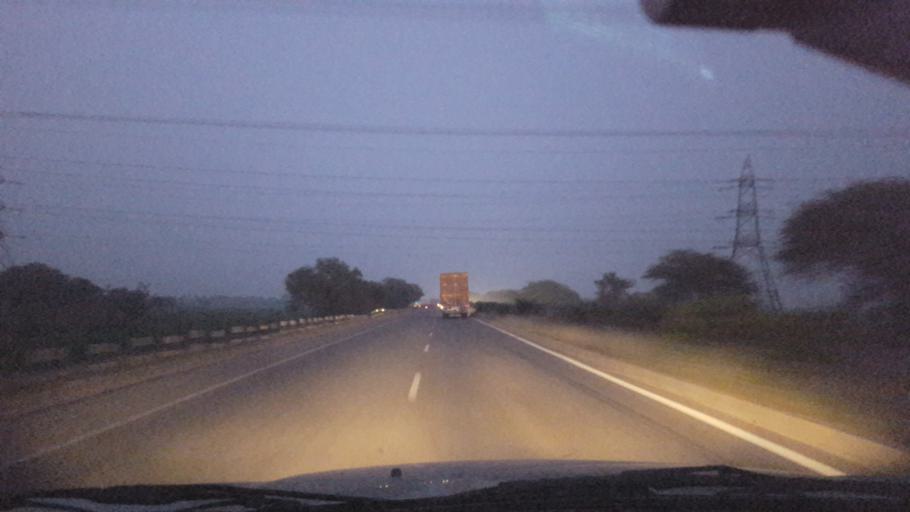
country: IN
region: Andhra Pradesh
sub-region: East Godavari
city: Rajahmundry
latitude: 17.1087
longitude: 81.9211
